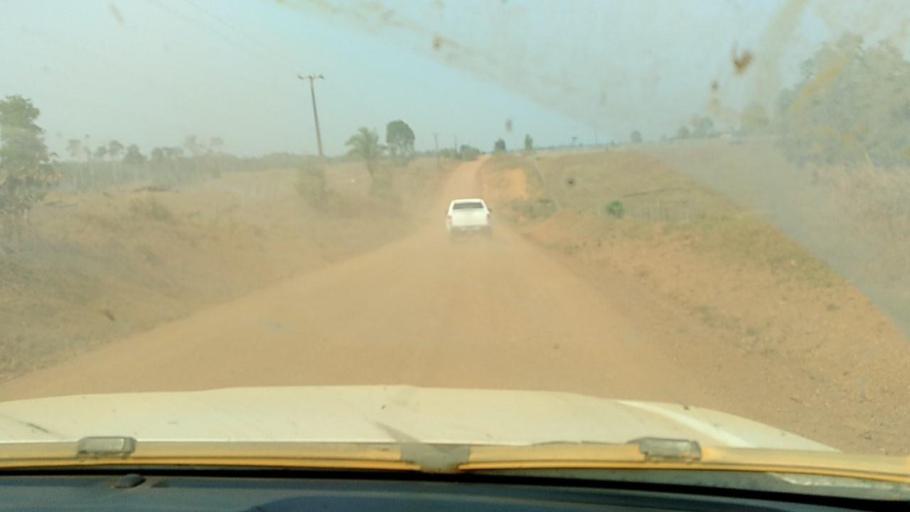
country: BR
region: Rondonia
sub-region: Porto Velho
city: Porto Velho
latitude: -8.8476
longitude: -64.1649
